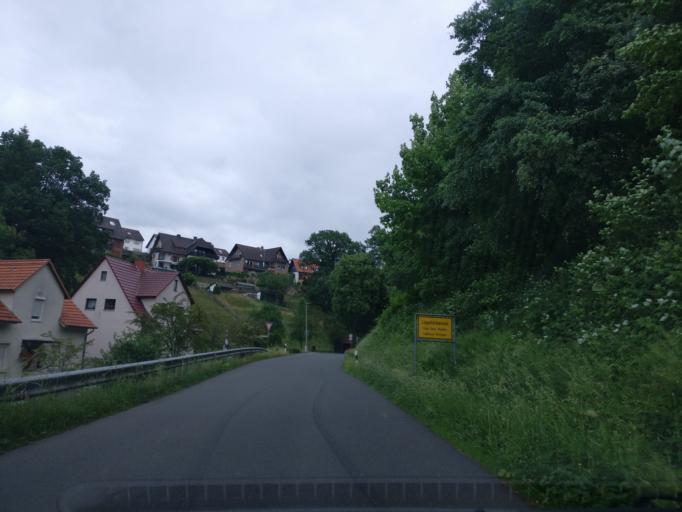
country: DE
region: Lower Saxony
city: Scheden
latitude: 51.4158
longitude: 9.7208
